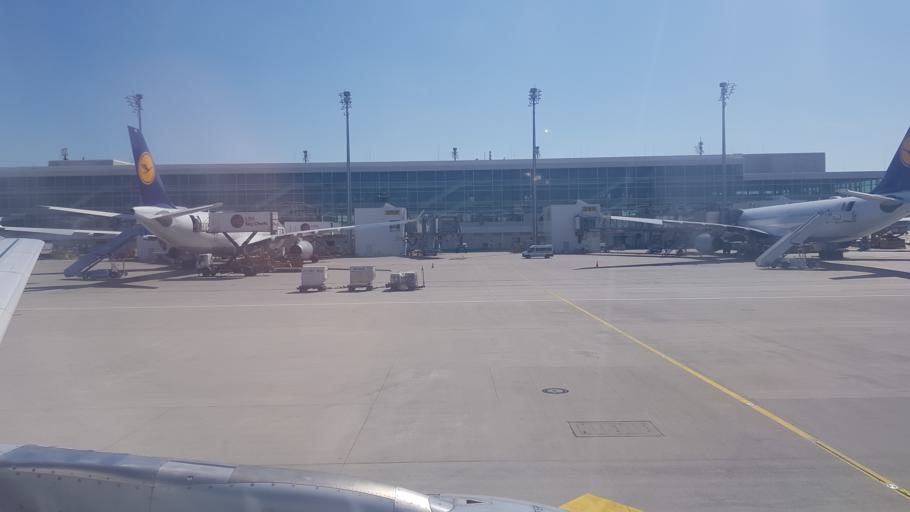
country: DE
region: Bavaria
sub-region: Upper Bavaria
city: Hallbergmoos
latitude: 48.3528
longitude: 11.7962
